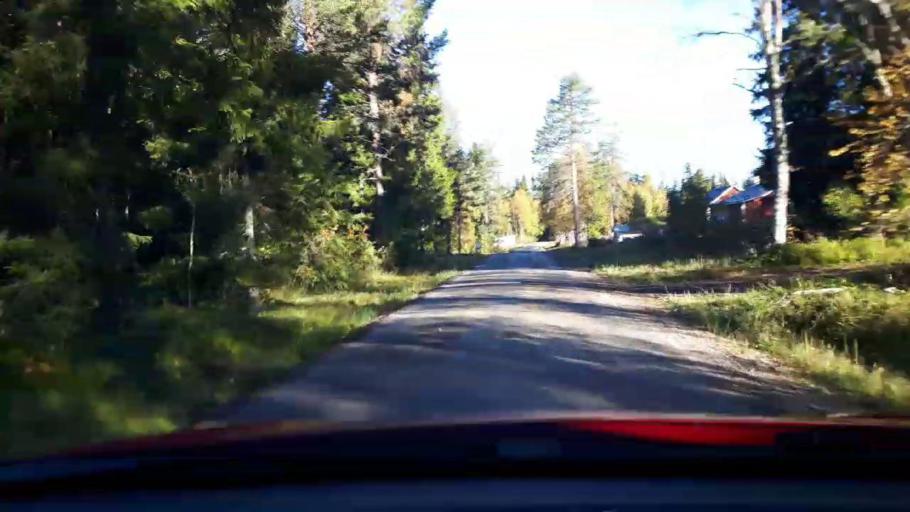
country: SE
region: Jaemtland
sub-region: Stroemsunds Kommun
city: Stroemsund
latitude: 64.3975
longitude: 15.1454
